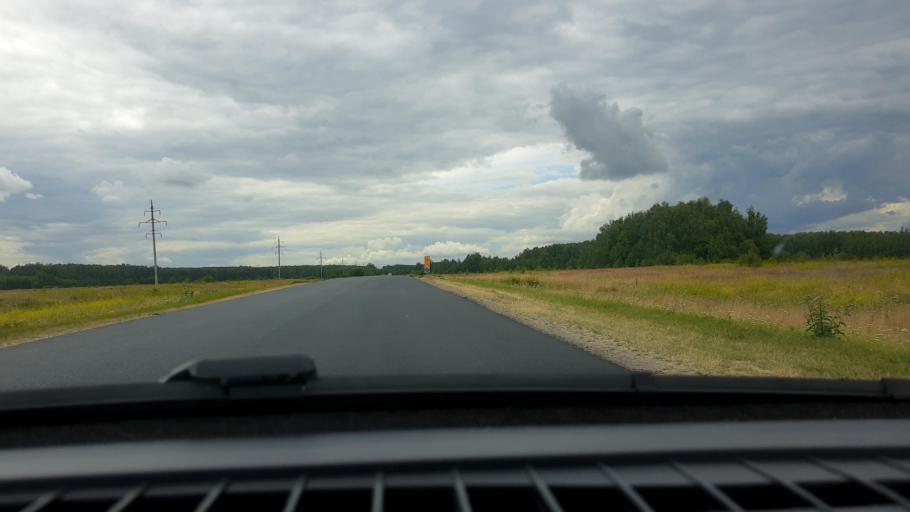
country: RU
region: Nizjnij Novgorod
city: Bol'shoye Murashkino
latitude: 55.8017
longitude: 44.8752
